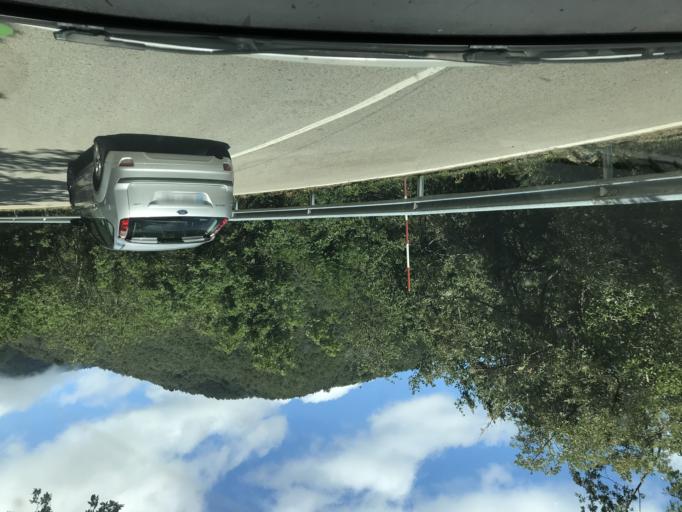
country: ES
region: Cantabria
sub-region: Provincia de Cantabria
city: Cabezon de Liebana
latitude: 43.0748
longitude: -4.4892
